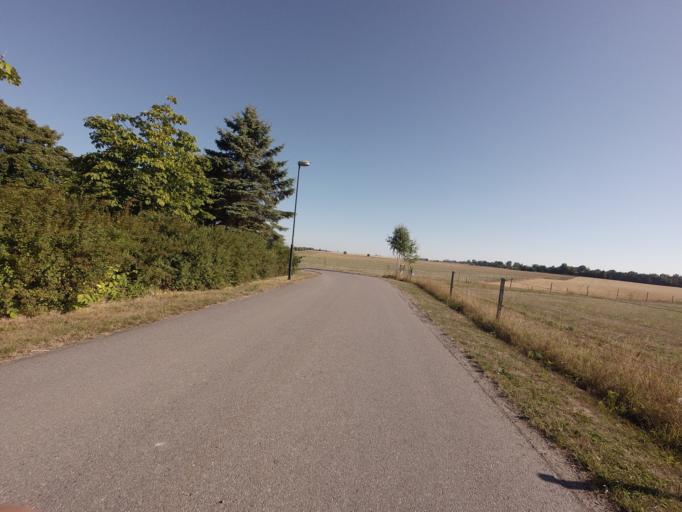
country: SE
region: Skane
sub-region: Trelleborgs Kommun
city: Trelleborg
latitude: 55.3919
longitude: 13.1102
